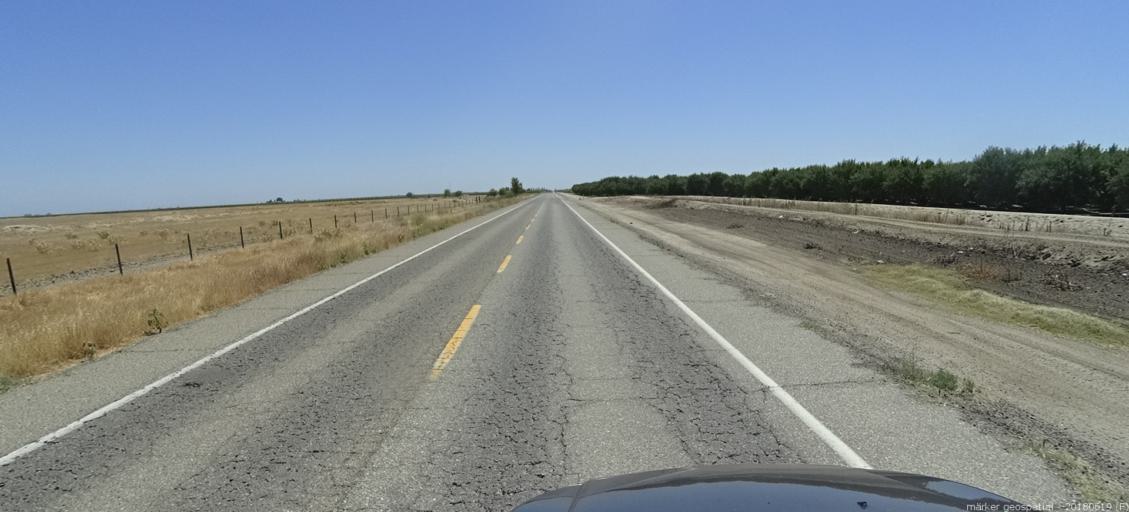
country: US
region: California
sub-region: Fresno County
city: Mendota
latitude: 36.8510
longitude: -120.2275
